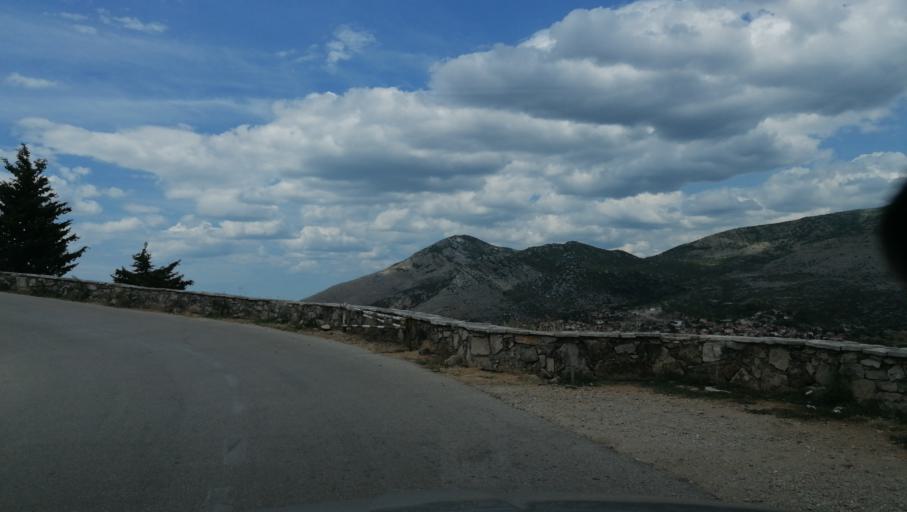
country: BA
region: Republika Srpska
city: Trebinje
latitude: 42.7118
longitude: 18.3605
